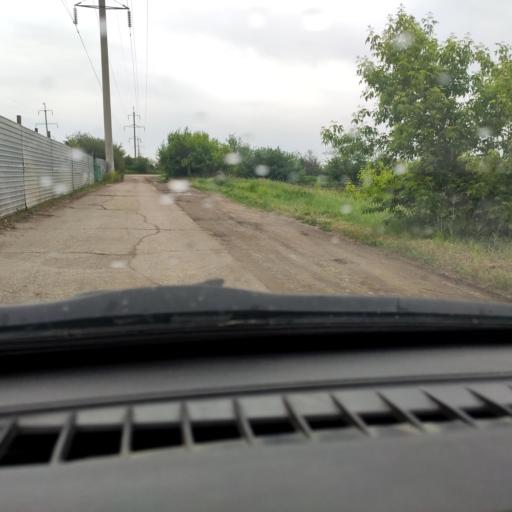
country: RU
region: Samara
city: Tol'yatti
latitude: 53.5877
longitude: 49.4354
